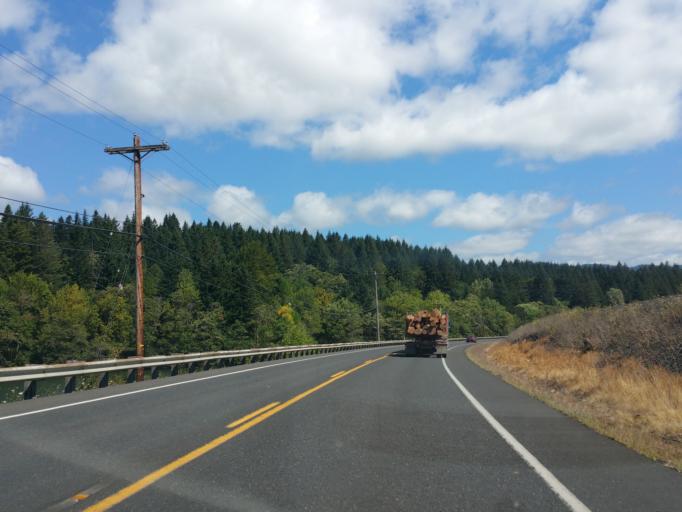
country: US
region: Oregon
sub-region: Hood River County
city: Cascade Locks
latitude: 45.6756
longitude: -121.9095
